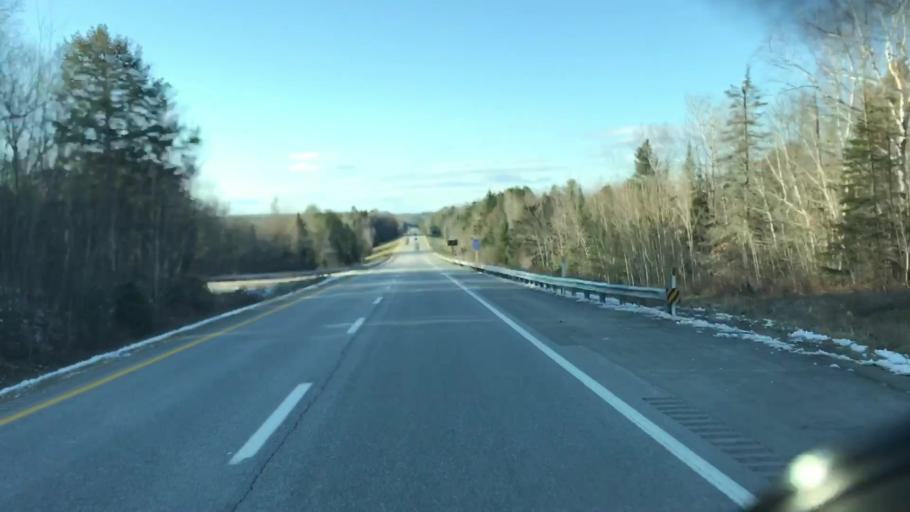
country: US
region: Maine
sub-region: Penobscot County
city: Carmel
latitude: 44.7621
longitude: -68.9845
